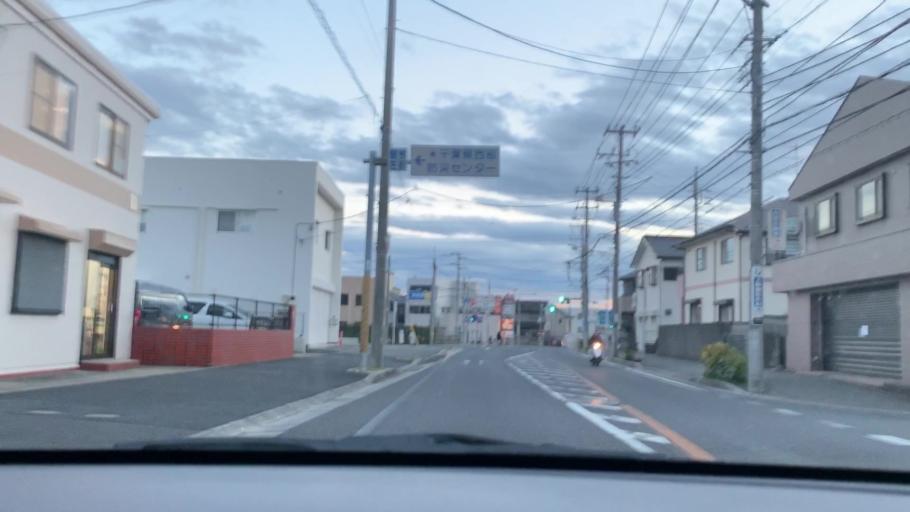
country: JP
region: Chiba
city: Matsudo
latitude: 35.7675
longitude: 139.8993
